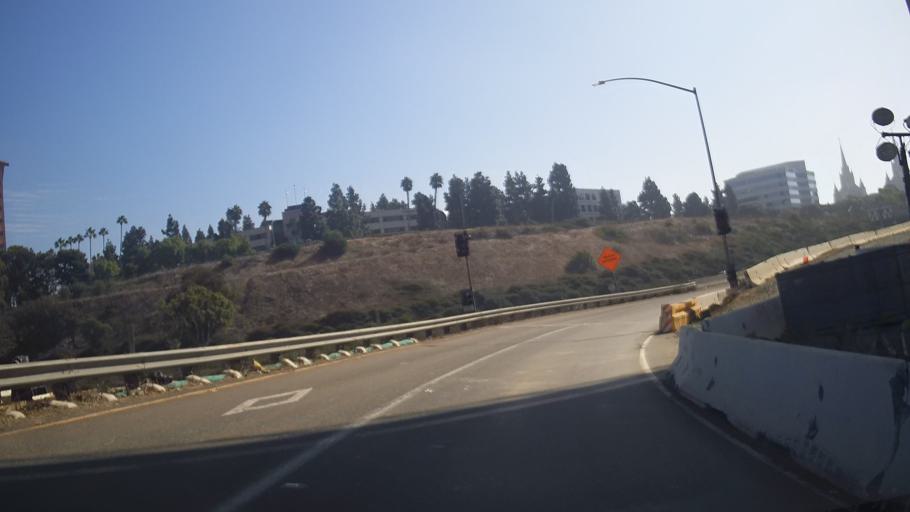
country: US
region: California
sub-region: San Diego County
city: La Jolla
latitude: 32.8714
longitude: -117.2300
